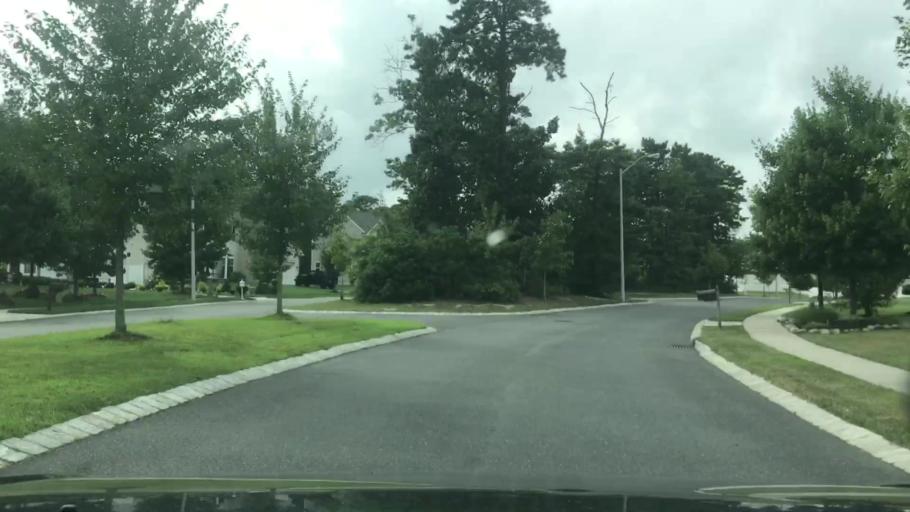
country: US
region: New Jersey
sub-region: Ocean County
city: Barnegat
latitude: 39.7520
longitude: -74.2406
